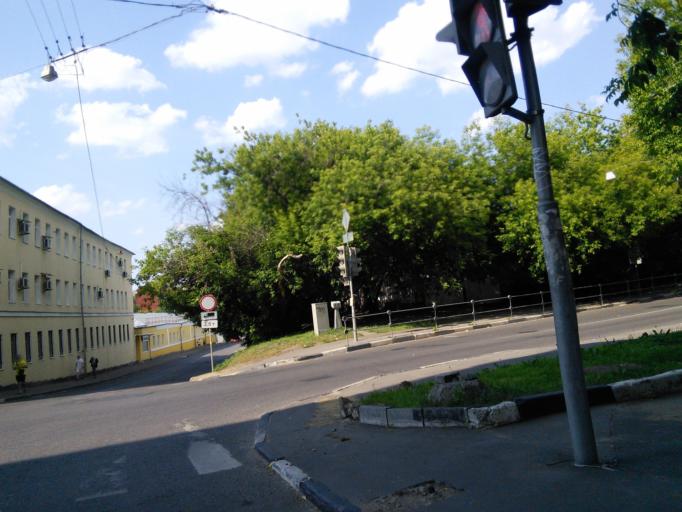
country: RU
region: Moscow
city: Lefortovo
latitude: 55.7846
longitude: 37.7102
